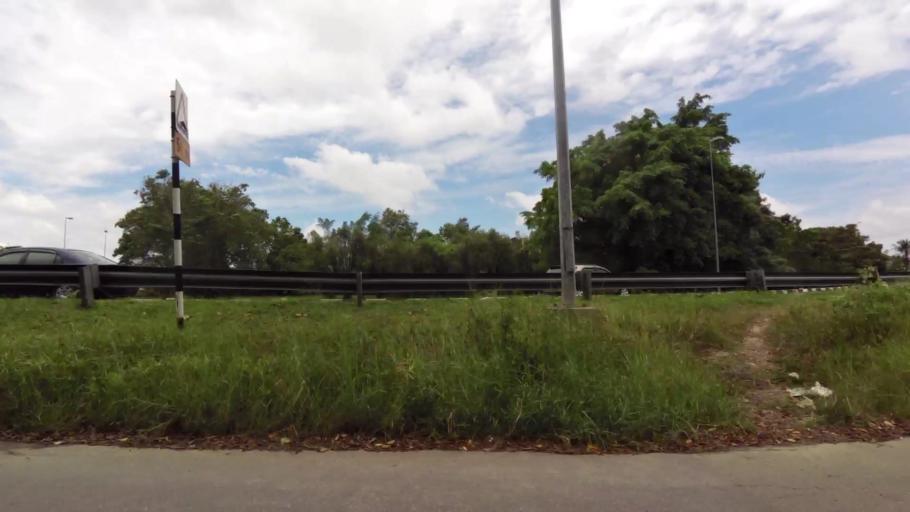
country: BN
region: Brunei and Muara
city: Bandar Seri Begawan
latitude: 4.9117
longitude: 114.9201
